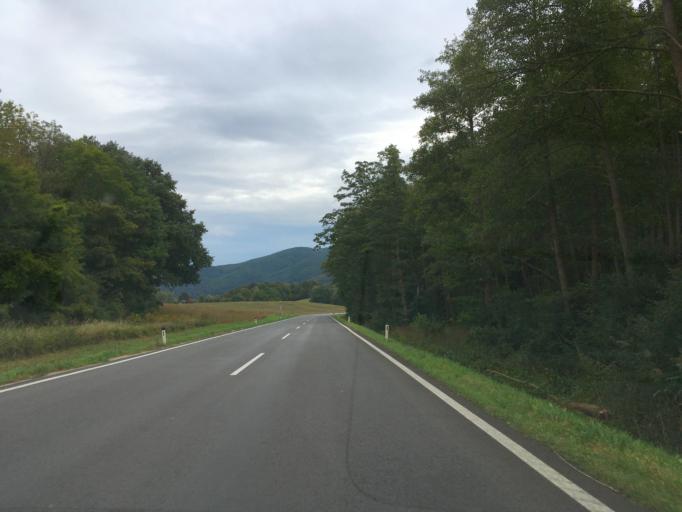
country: AT
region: Lower Austria
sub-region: Politischer Bezirk Modling
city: Gaaden
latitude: 48.0538
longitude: 16.1859
